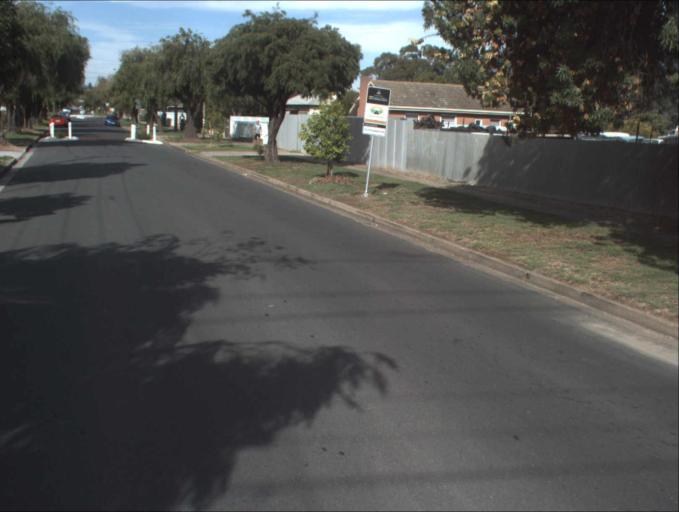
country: AU
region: South Australia
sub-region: Port Adelaide Enfield
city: Blair Athol
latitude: -34.8635
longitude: 138.5835
